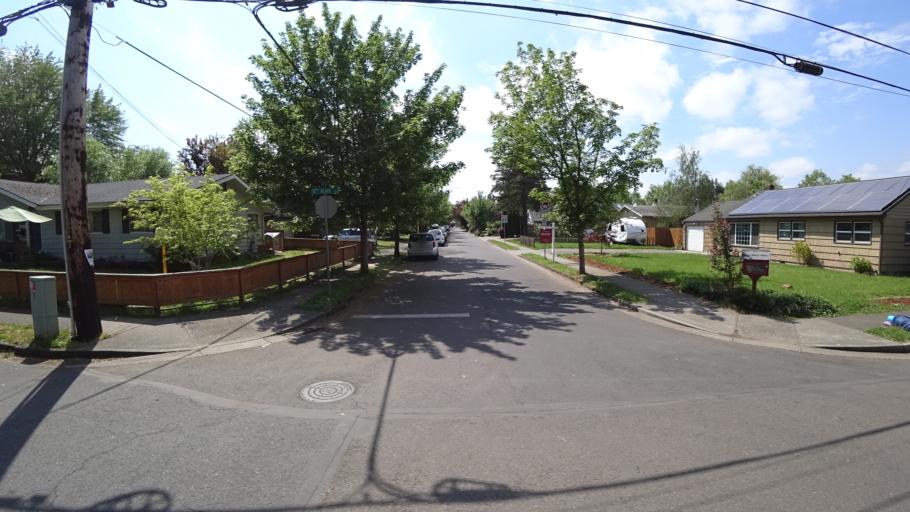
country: US
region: Oregon
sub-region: Washington County
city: Beaverton
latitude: 45.4806
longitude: -122.7966
